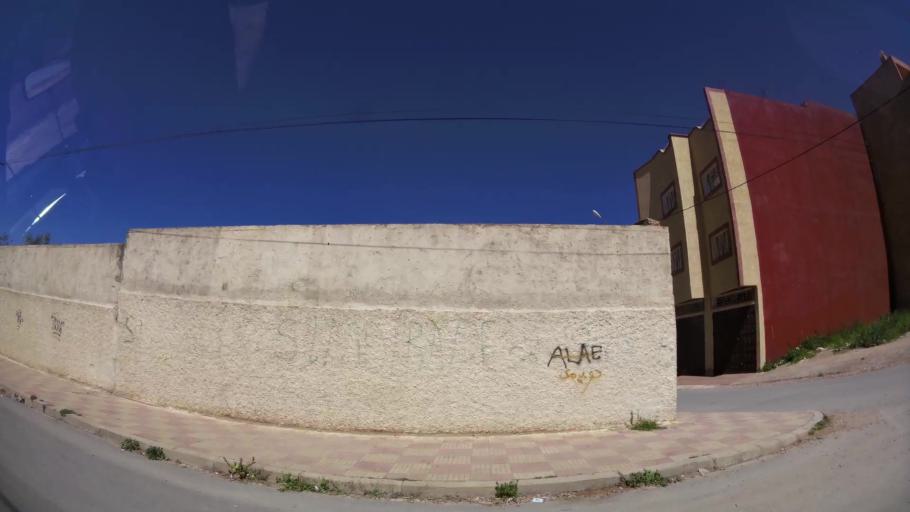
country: MA
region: Oriental
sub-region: Oujda-Angad
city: Oujda
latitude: 34.6648
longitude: -1.8741
